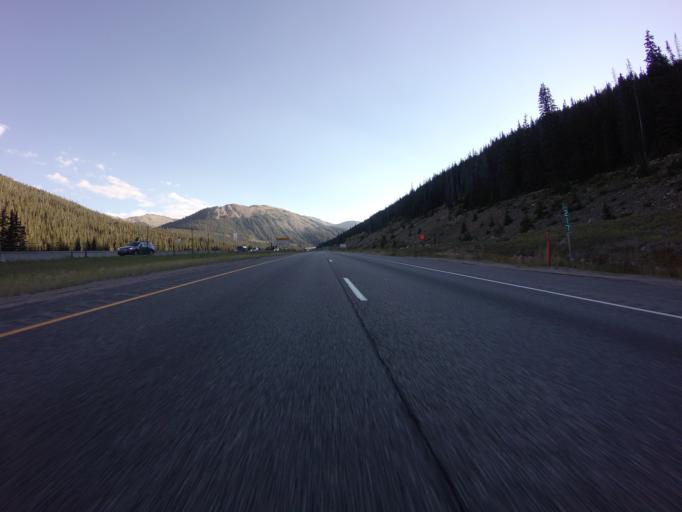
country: US
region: Colorado
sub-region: Summit County
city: Keystone
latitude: 39.6926
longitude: -105.8783
